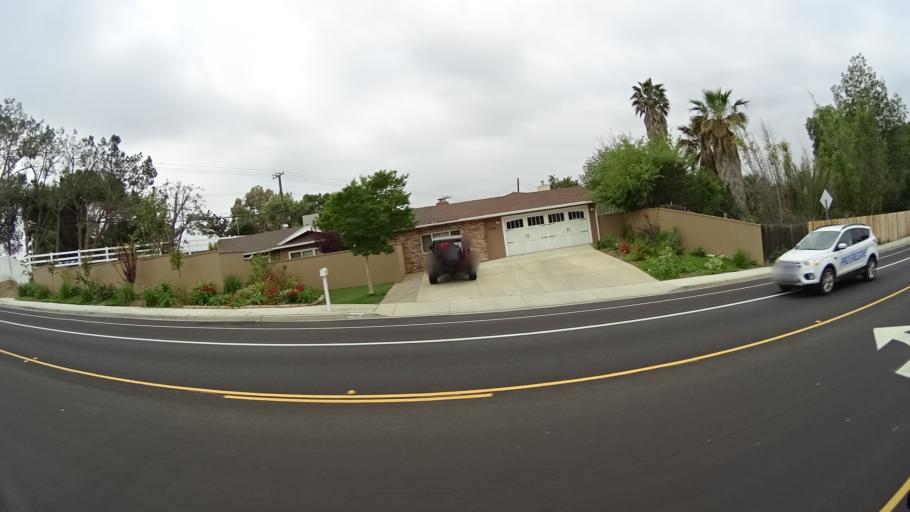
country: US
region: California
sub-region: Ventura County
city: Thousand Oaks
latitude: 34.2061
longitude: -118.8577
